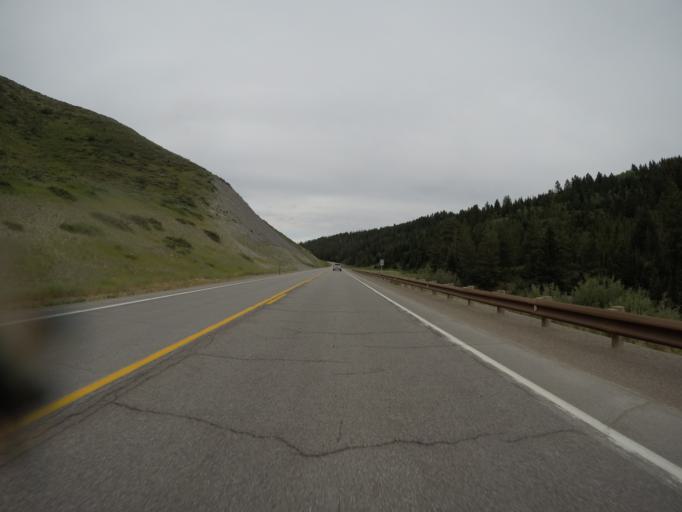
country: US
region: Wyoming
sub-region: Lincoln County
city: Afton
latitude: 42.4863
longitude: -110.9362
